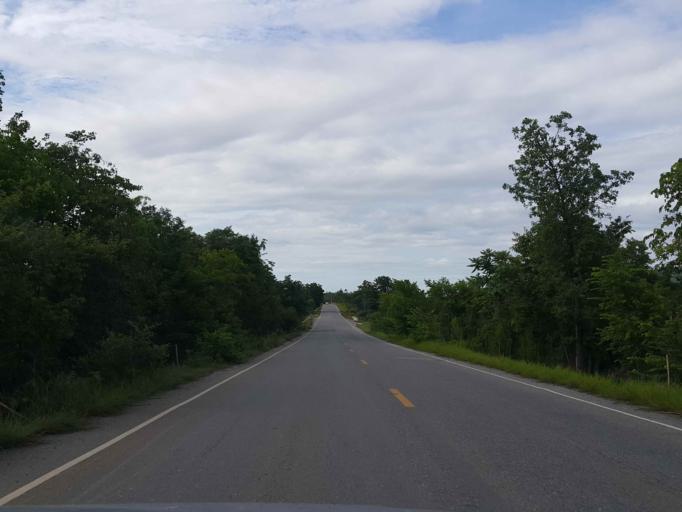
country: TH
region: Sukhothai
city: Thung Saliam
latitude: 17.2426
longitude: 99.5160
